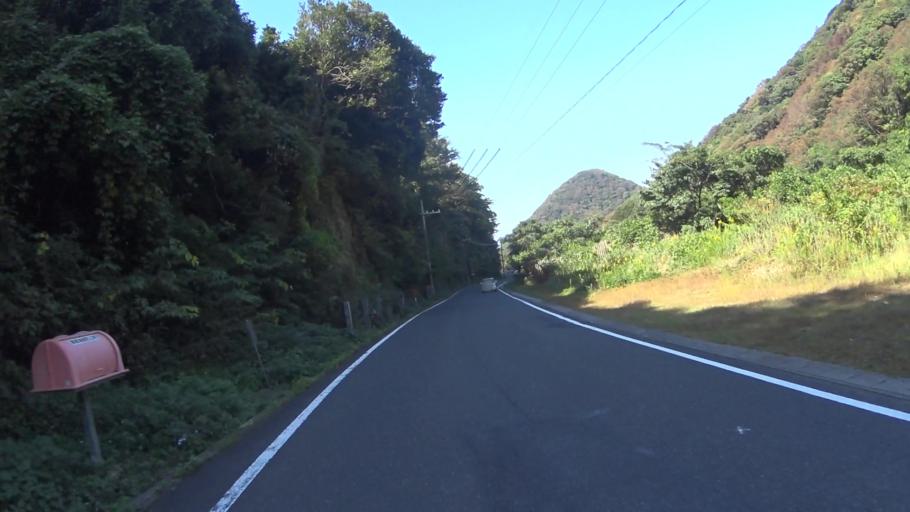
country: JP
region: Kyoto
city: Miyazu
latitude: 35.7678
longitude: 135.2278
